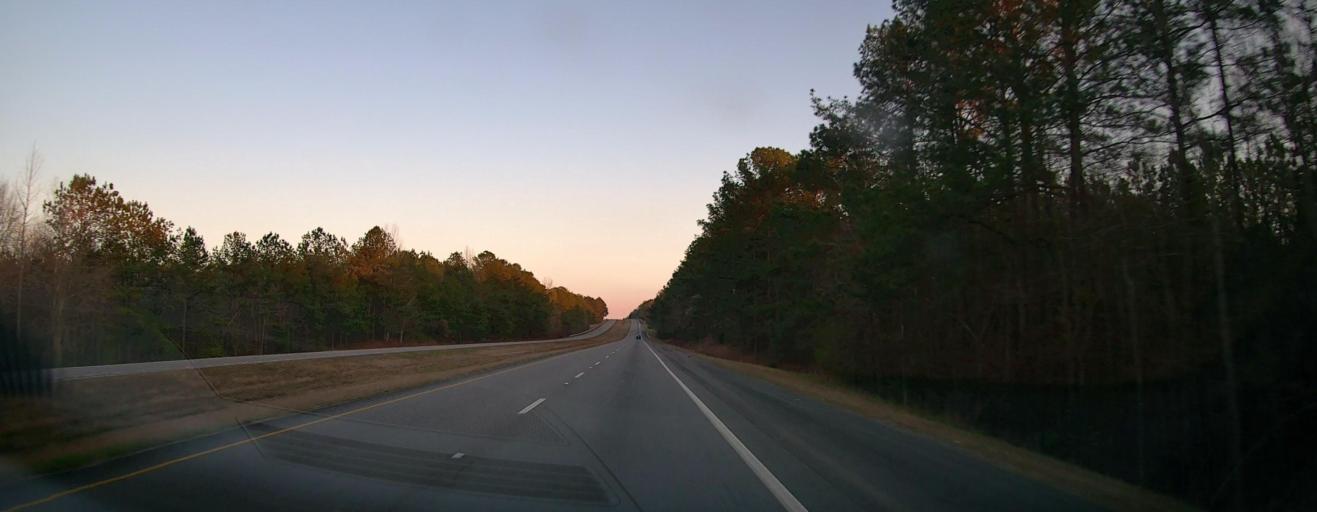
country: US
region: Alabama
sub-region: Coosa County
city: Goodwater
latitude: 33.0274
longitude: -86.1117
